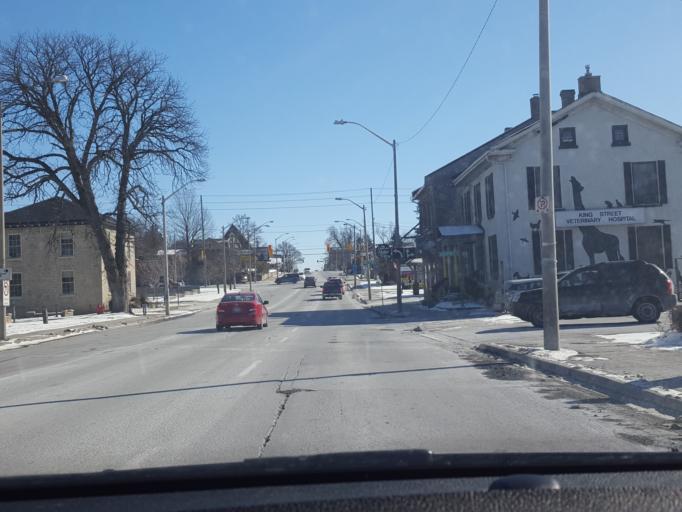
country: CA
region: Ontario
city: Cambridge
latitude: 43.3993
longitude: -80.3650
